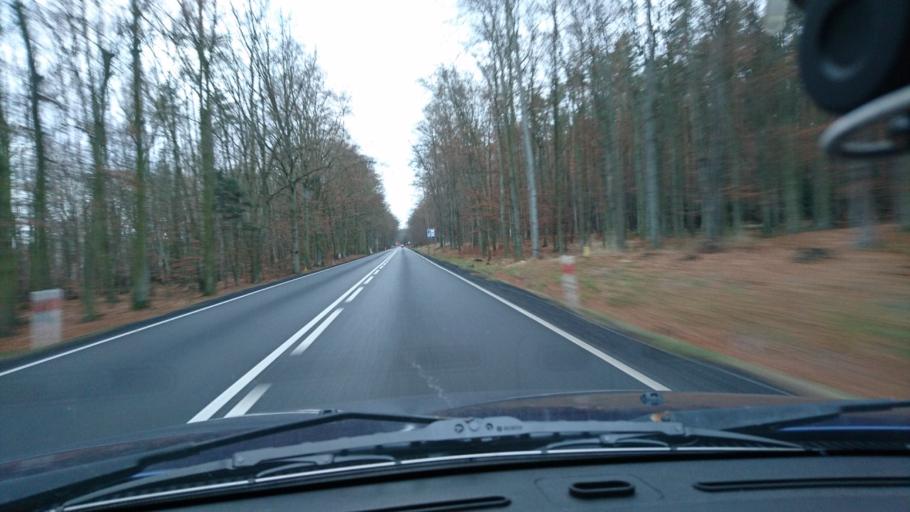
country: PL
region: Opole Voivodeship
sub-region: Powiat kluczborski
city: Kluczbork
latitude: 50.9619
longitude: 18.2879
